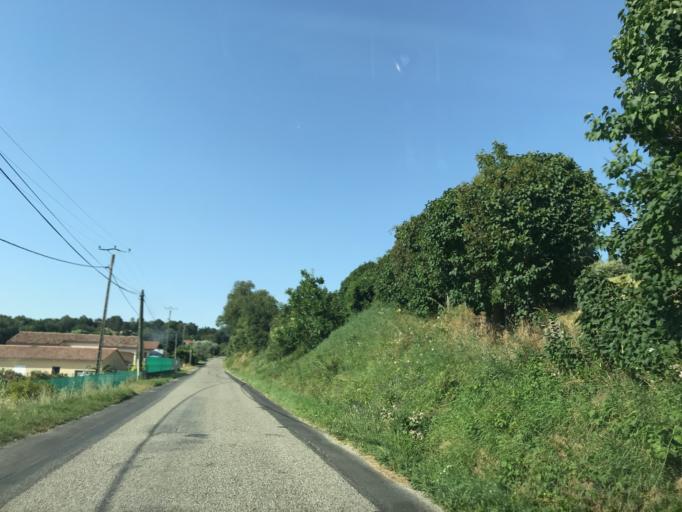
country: FR
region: Rhone-Alpes
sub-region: Departement de la Drome
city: Clerieux
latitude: 45.1303
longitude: 4.9888
